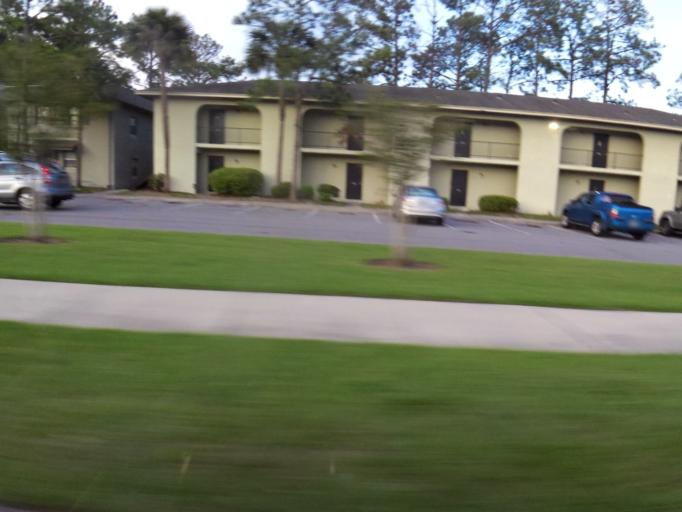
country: US
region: Florida
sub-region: Duval County
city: Jacksonville
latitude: 30.2714
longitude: -81.6072
